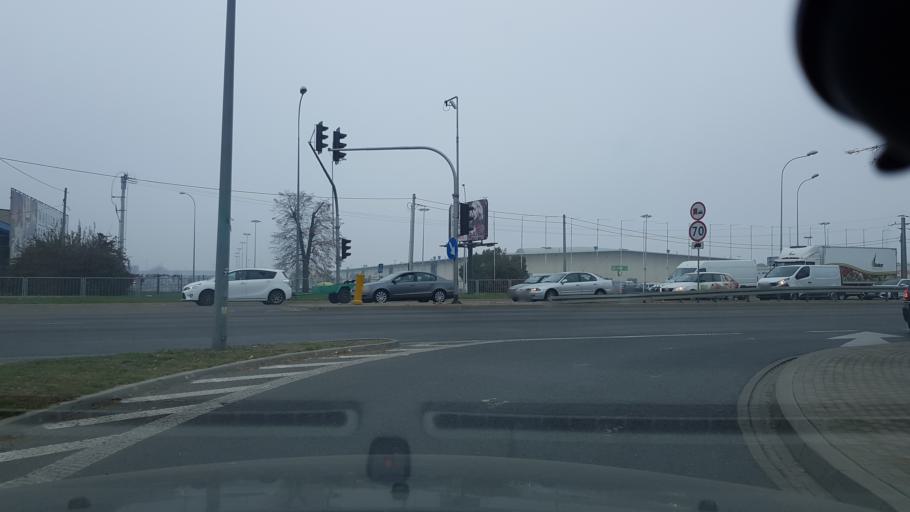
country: PL
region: Masovian Voivodeship
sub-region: Powiat pruszkowski
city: Piastow
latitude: 52.2143
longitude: 20.8399
